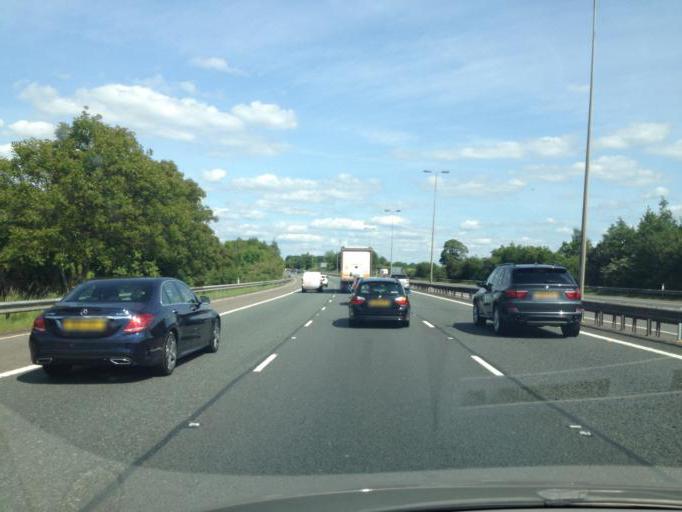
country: GB
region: England
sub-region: Buckinghamshire
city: High Wycombe
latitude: 51.6102
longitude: -0.7882
